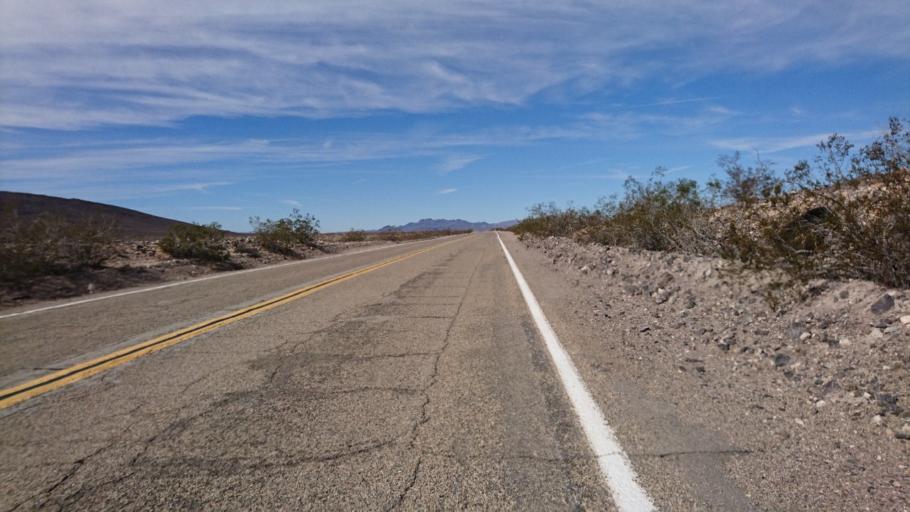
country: US
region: California
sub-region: San Bernardino County
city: Twentynine Palms
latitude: 34.6994
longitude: -116.0624
